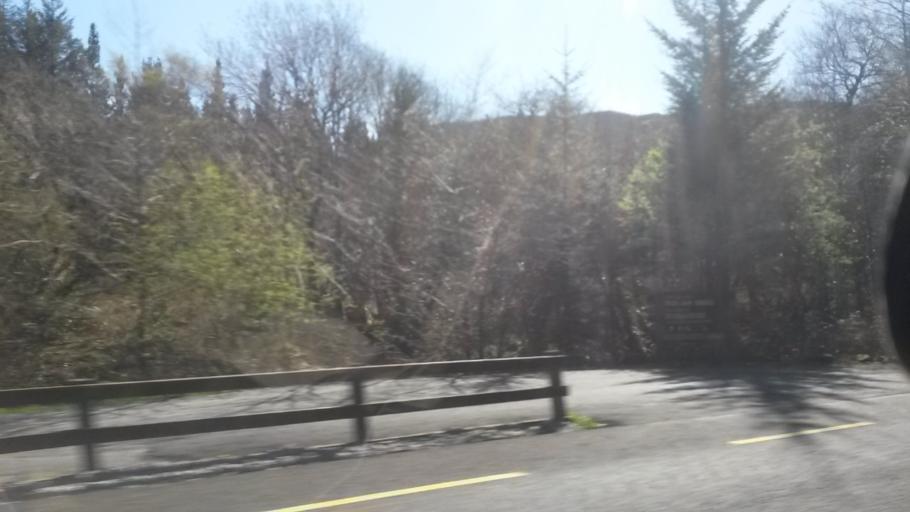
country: IE
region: Munster
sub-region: Ciarrai
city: Cill Airne
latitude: 51.9534
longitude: -9.3894
